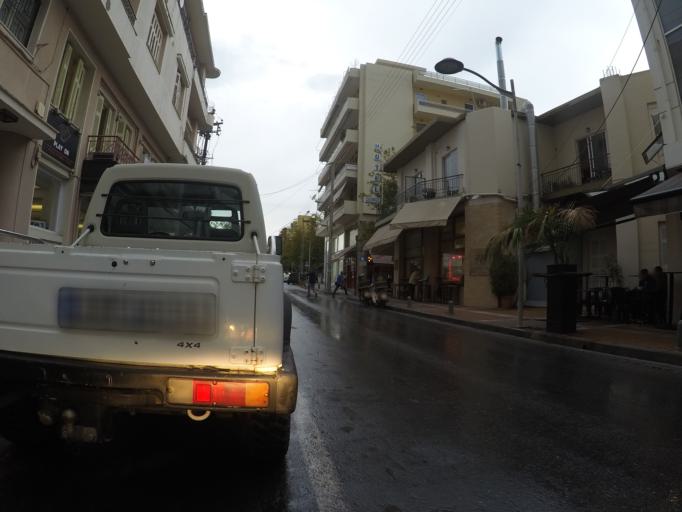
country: GR
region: Peloponnese
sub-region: Nomos Messinias
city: Kalamata
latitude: 37.0374
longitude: 22.1100
